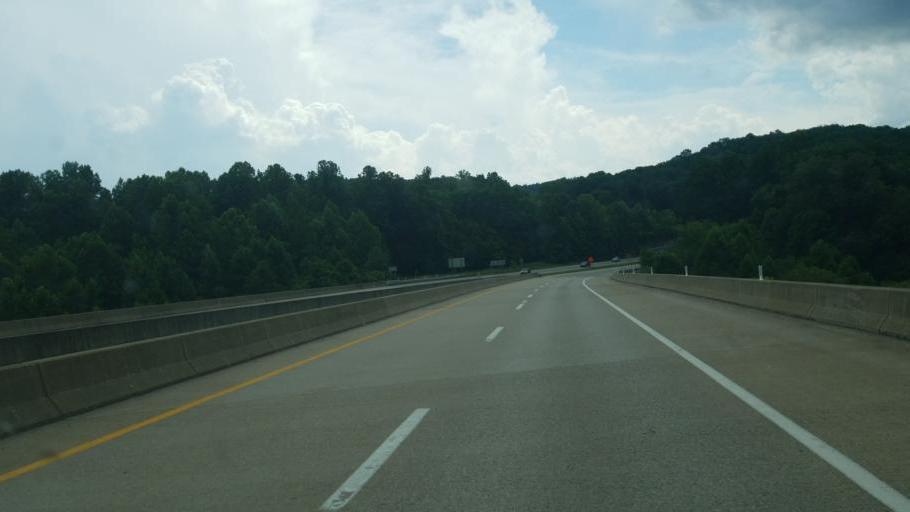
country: US
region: West Virginia
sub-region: Kanawha County
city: Alum Creek
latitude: 38.2680
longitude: -81.7891
